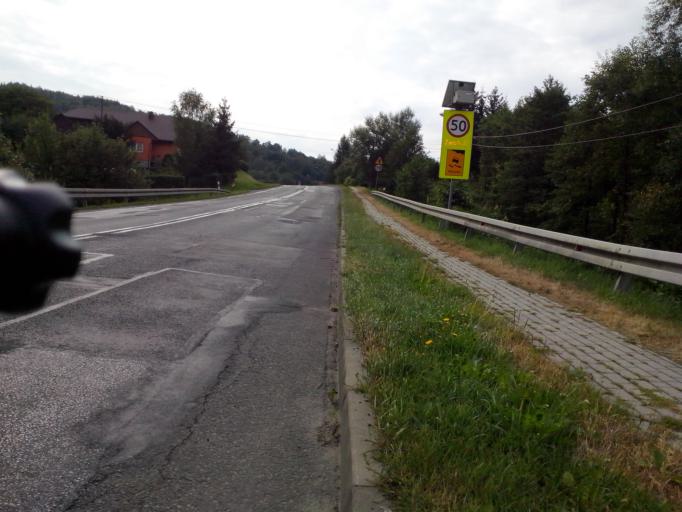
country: PL
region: Subcarpathian Voivodeship
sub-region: Powiat brzozowski
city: Domaradz
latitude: 49.7850
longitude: 21.9473
